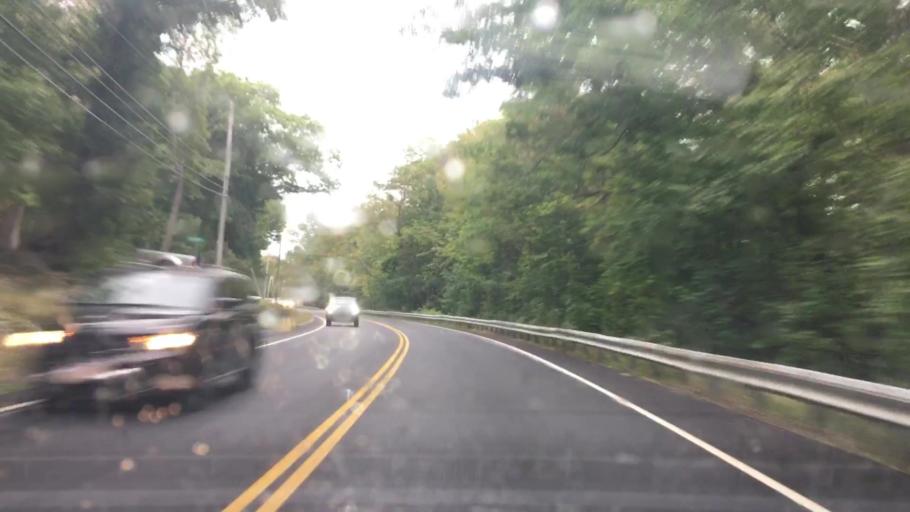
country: US
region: Maine
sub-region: Penobscot County
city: Orrington
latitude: 44.6796
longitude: -68.8074
